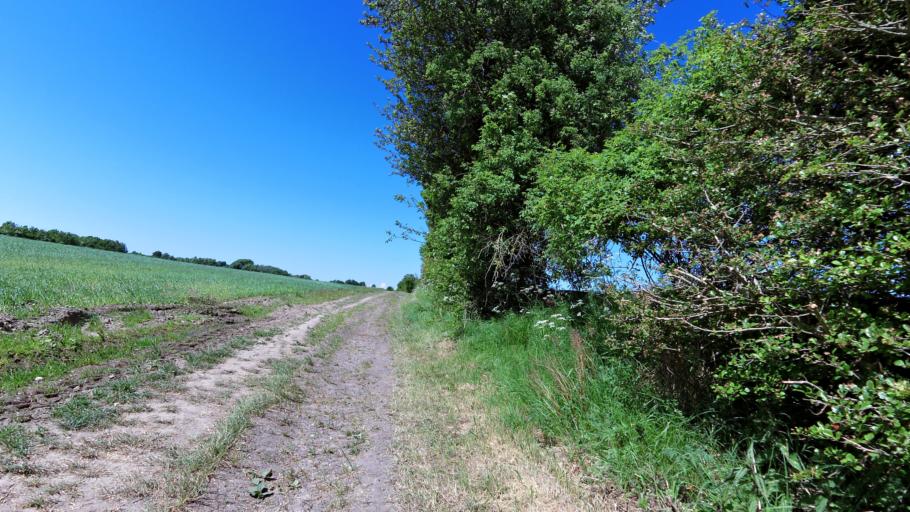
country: DK
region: Central Jutland
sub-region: Arhus Kommune
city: Framlev
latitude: 56.1369
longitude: 10.0068
